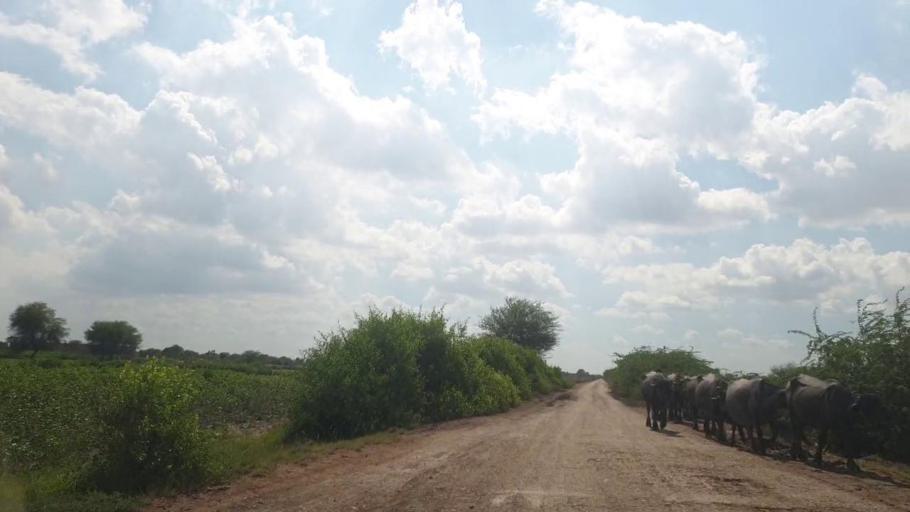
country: PK
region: Sindh
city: Pithoro
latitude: 25.5772
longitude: 69.3809
